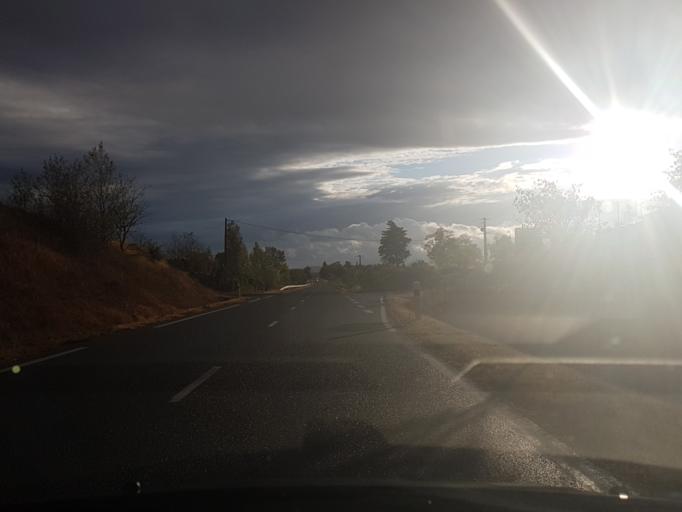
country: FR
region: Languedoc-Roussillon
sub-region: Departement de l'Aude
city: Bram
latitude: 43.1801
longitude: 2.0251
